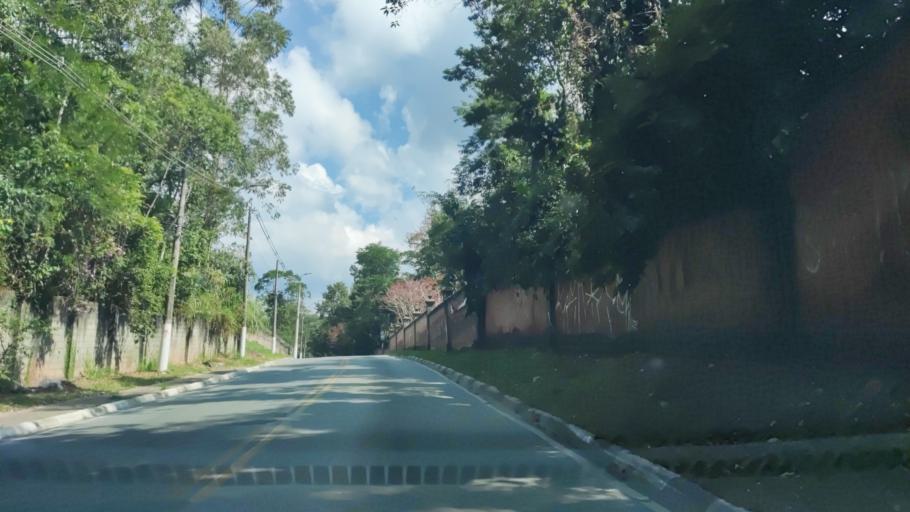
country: BR
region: Sao Paulo
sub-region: Itapecerica Da Serra
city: Itapecerica da Serra
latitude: -23.6945
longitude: -46.8266
